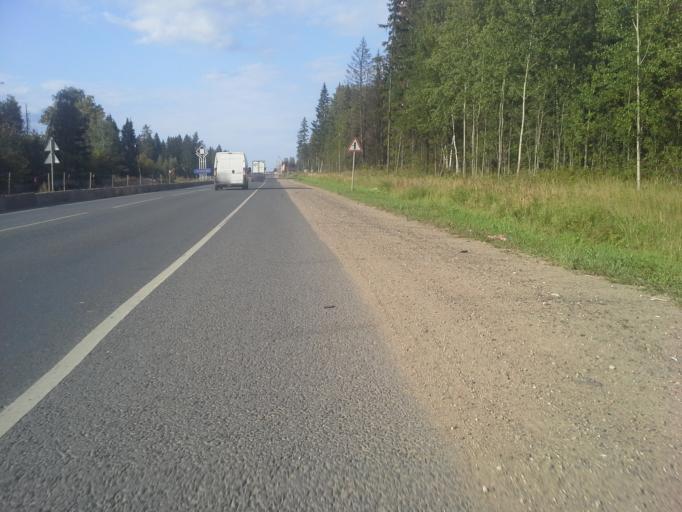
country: RU
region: Moskovskaya
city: Golitsyno
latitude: 55.5757
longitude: 36.9993
